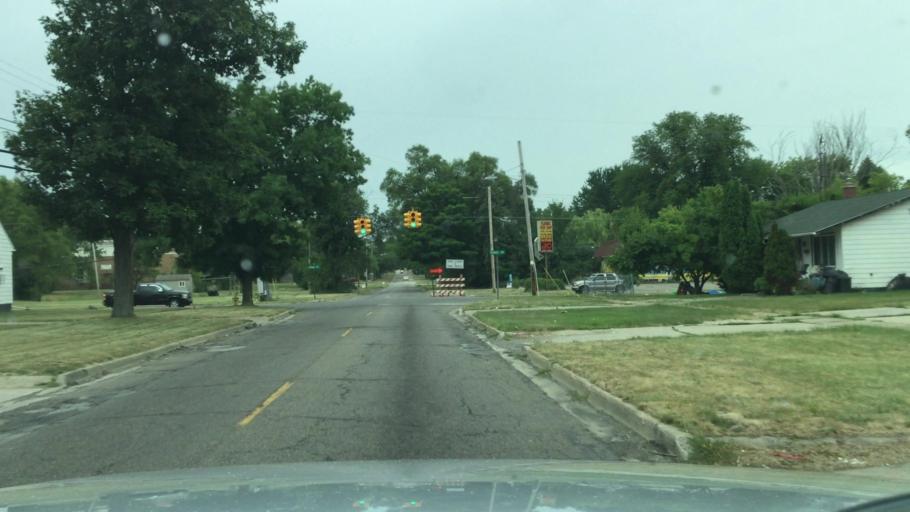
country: US
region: Michigan
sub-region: Genesee County
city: Beecher
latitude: 43.0545
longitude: -83.7236
